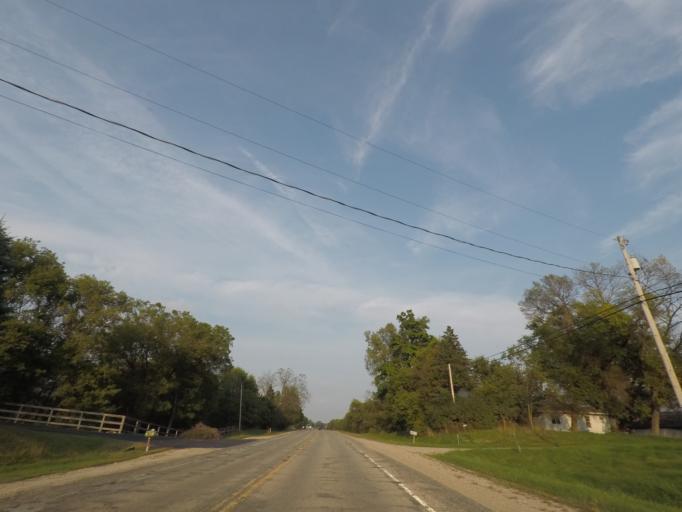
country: US
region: Wisconsin
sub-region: Dane County
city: Cottage Grove
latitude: 43.0861
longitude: -89.2529
